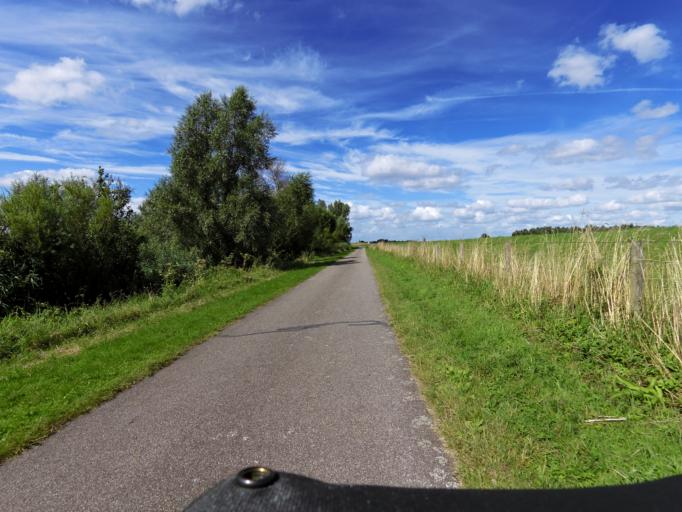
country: NL
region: South Holland
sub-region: Gemeente Zwijndrecht
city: Heerjansdam
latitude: 51.8216
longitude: 4.5632
